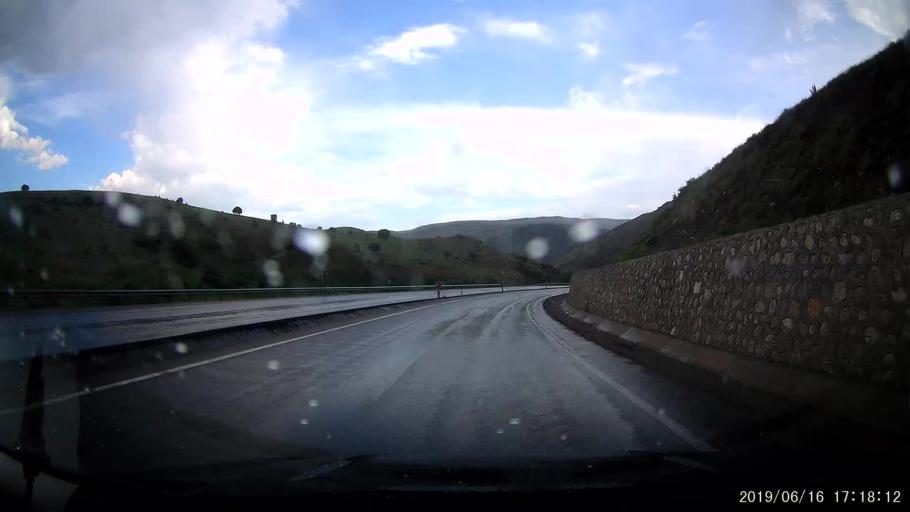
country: TR
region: Erzincan
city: Tercan
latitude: 39.8173
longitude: 40.5296
